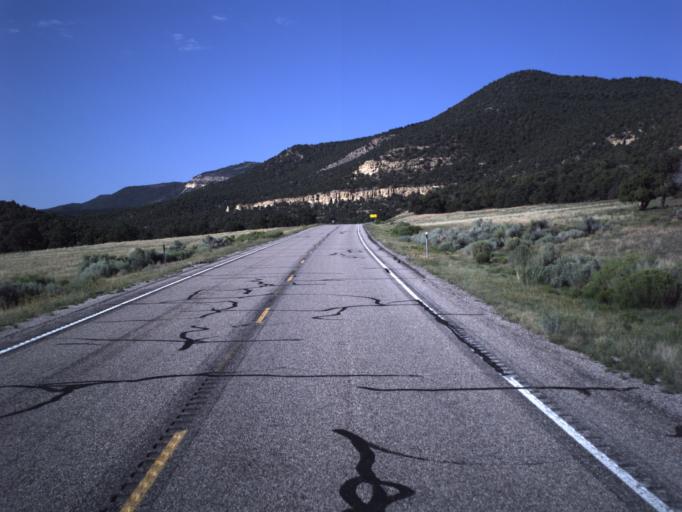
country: US
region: Utah
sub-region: Wayne County
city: Loa
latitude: 38.7494
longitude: -111.3905
